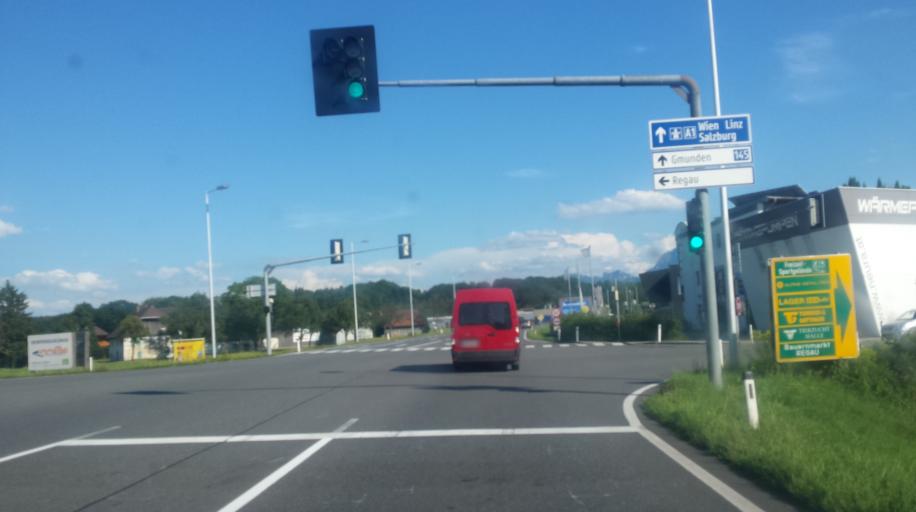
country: AT
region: Upper Austria
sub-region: Politischer Bezirk Vocklabruck
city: Attnang-Puchheim
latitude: 47.9865
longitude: 13.6943
